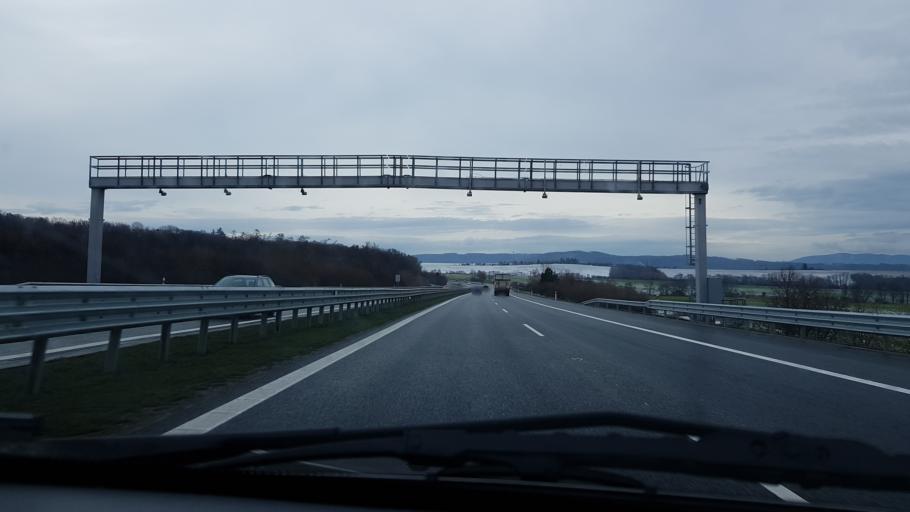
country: CZ
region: Olomoucky
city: Dolni Ujezd
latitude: 49.5489
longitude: 17.5497
